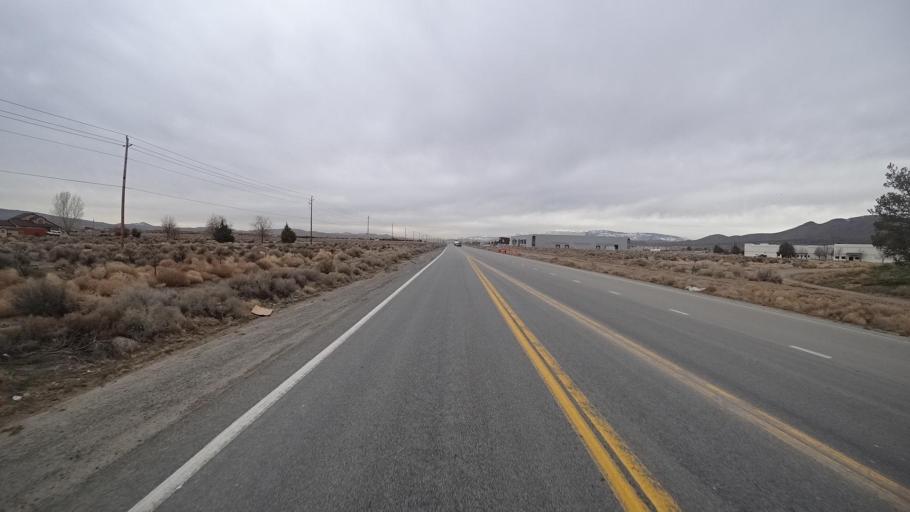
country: US
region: Nevada
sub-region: Washoe County
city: Spanish Springs
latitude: 39.6717
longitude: -119.7021
